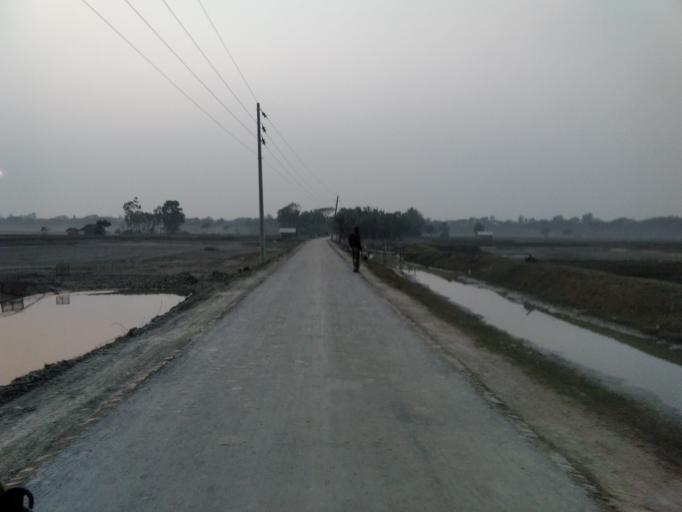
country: BD
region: Khulna
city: Satkhira
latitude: 22.6501
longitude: 89.0041
